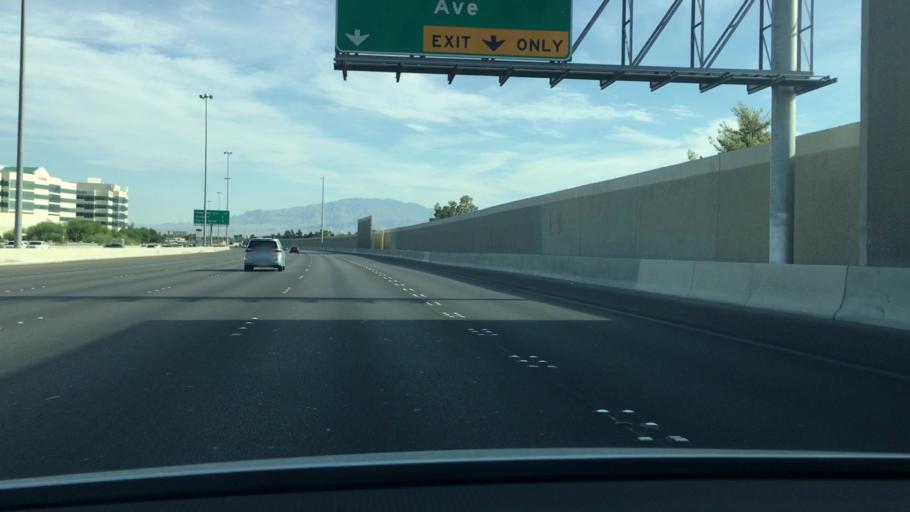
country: US
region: Nevada
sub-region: Clark County
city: Spring Valley
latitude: 36.2054
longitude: -115.2444
